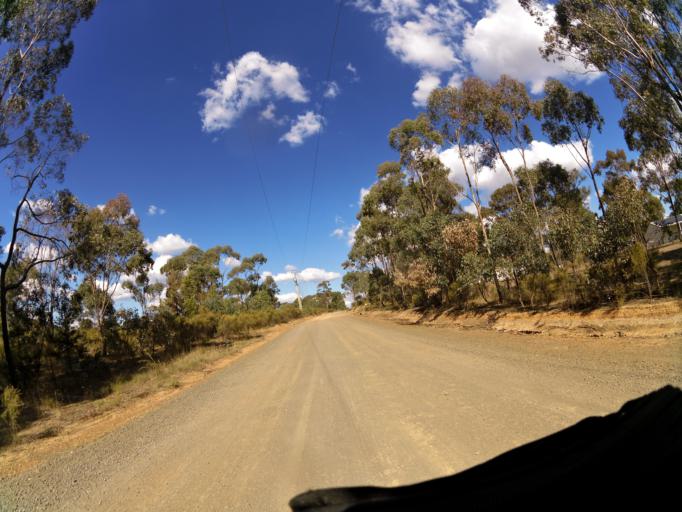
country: AU
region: Victoria
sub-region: Greater Bendigo
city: Kennington
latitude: -36.9529
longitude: 144.7757
